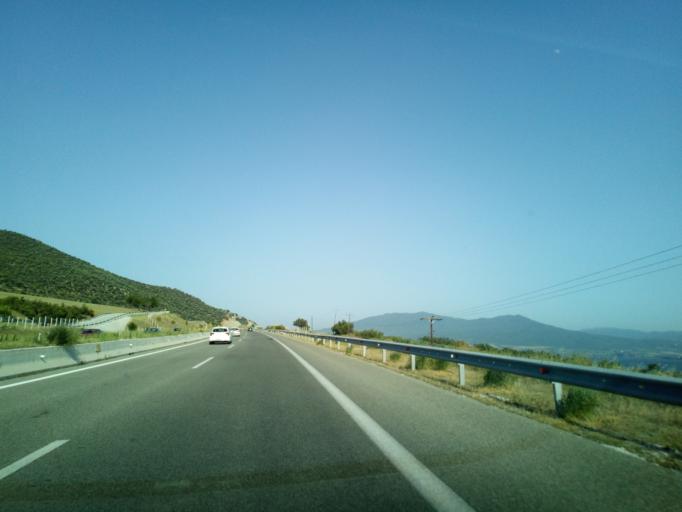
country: GR
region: Central Macedonia
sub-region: Nomos Thessalonikis
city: Nea Apollonia
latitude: 40.6836
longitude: 23.5521
